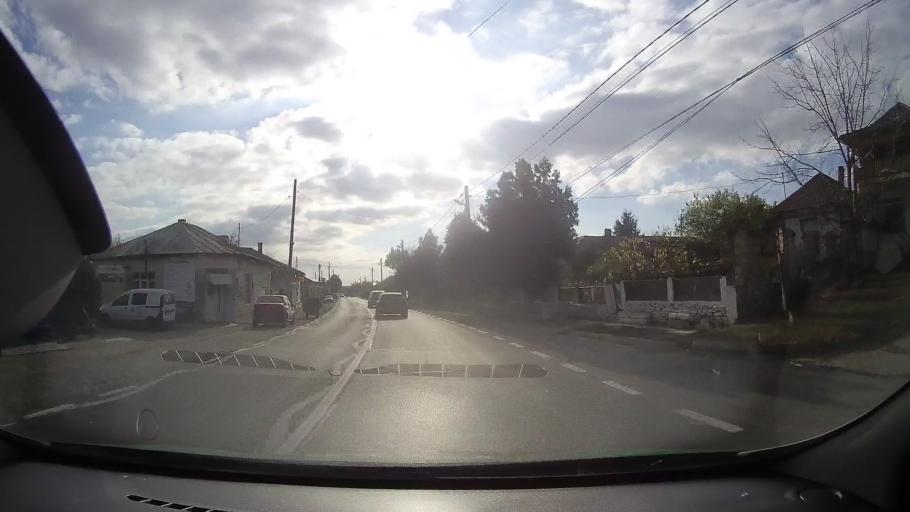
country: RO
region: Tulcea
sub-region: Comuna Topolog
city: Topolog
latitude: 44.8799
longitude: 28.3762
